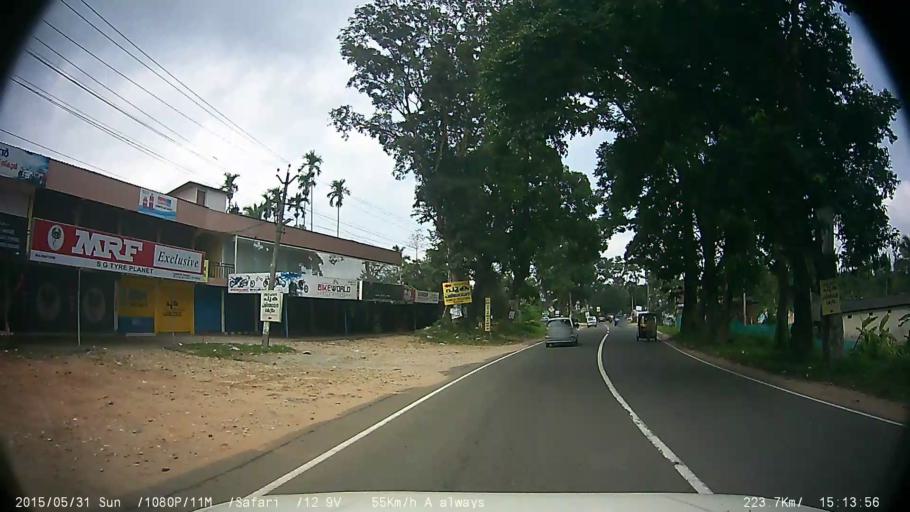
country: IN
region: Kerala
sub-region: Wayanad
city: Panamaram
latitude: 11.6608
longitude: 76.2422
